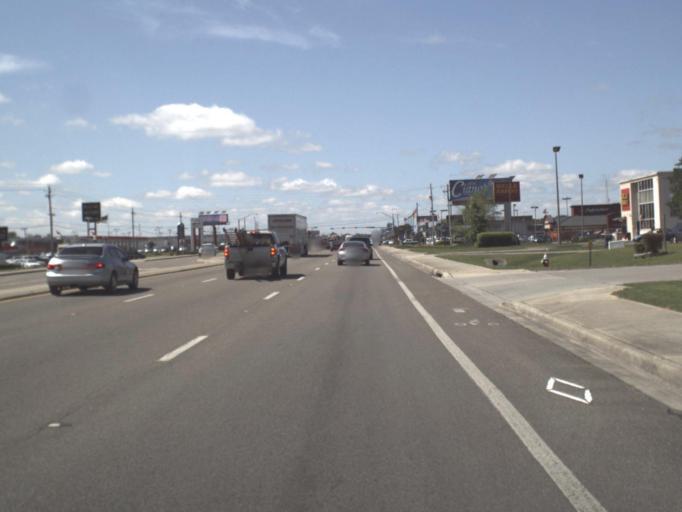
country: US
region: Florida
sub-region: Escambia County
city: Brent
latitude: 30.4722
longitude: -87.2461
